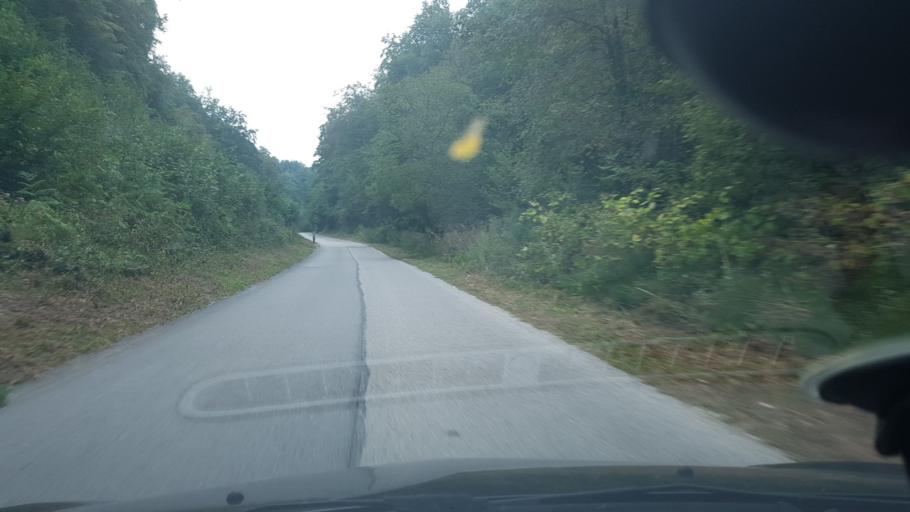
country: SI
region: Krsko
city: Senovo
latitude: 46.0217
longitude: 15.5049
